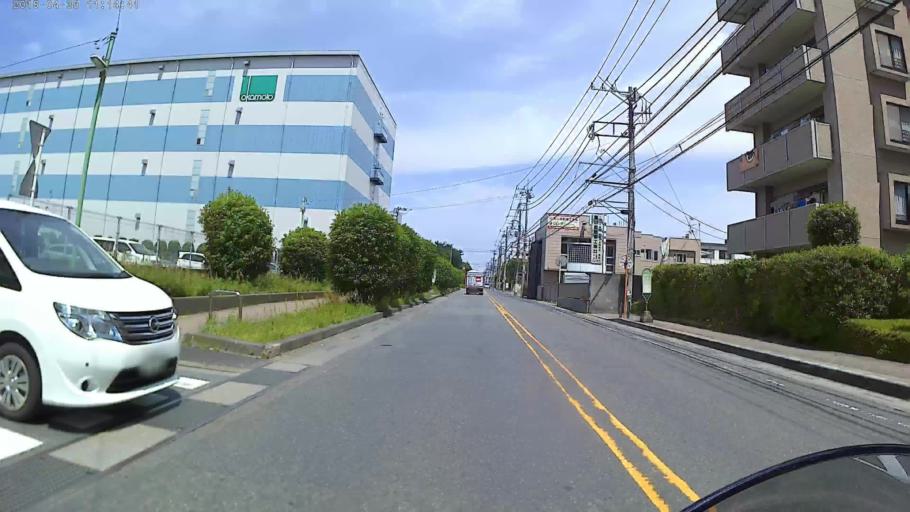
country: JP
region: Kanagawa
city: Minami-rinkan
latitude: 35.4757
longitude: 139.4316
